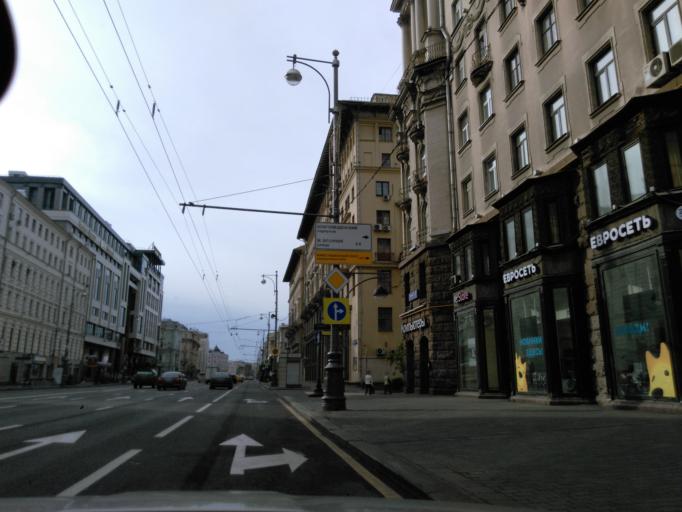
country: RU
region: Moscow
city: Moscow
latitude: 55.7683
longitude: 37.5985
